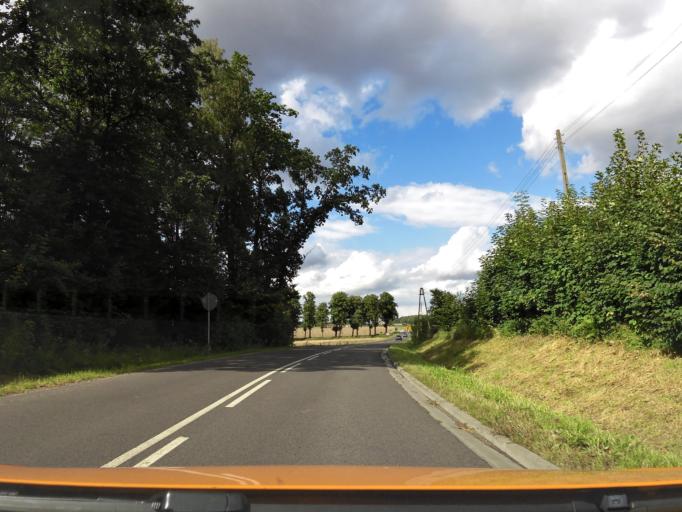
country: PL
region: West Pomeranian Voivodeship
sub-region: Powiat kolobrzeski
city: Ryman
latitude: 53.9692
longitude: 15.4901
